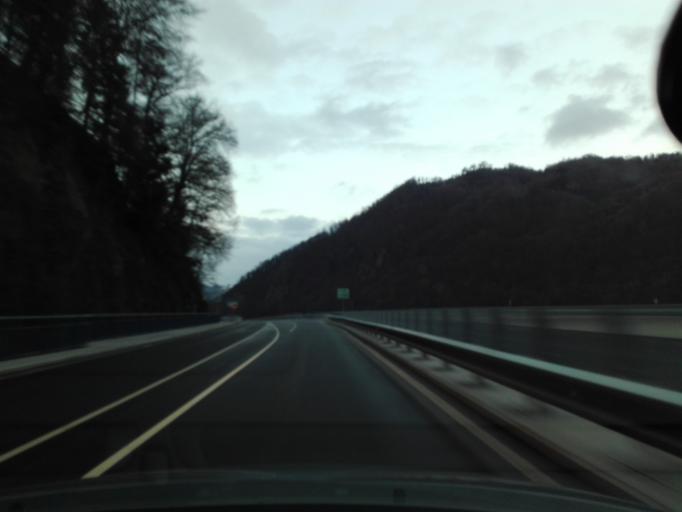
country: AT
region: Upper Austria
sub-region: Politischer Bezirk Perg
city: Bad Kreuzen
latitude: 48.2105
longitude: 14.8543
